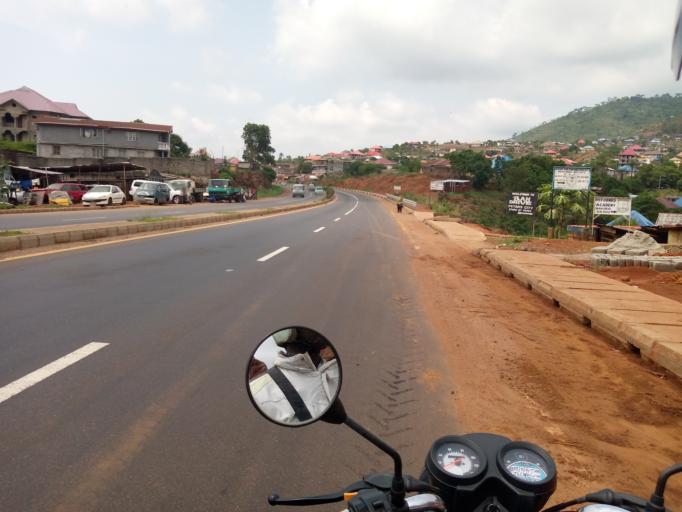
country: SL
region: Western Area
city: Waterloo
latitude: 8.3607
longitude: -13.0833
